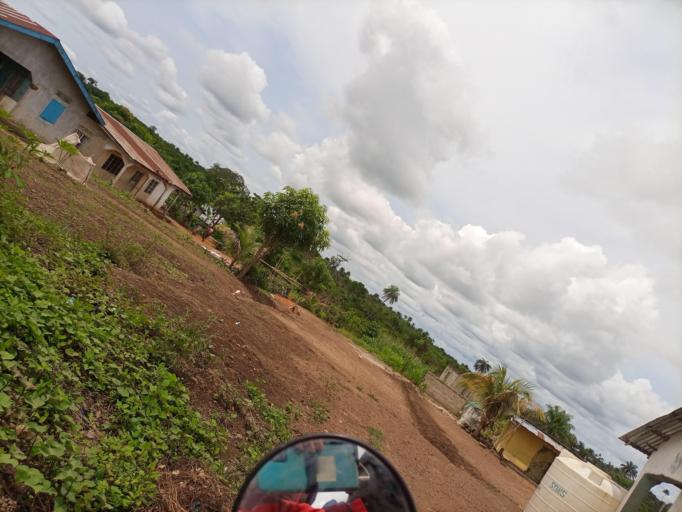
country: SL
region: Southern Province
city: Baoma
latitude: 7.9714
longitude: -11.7115
